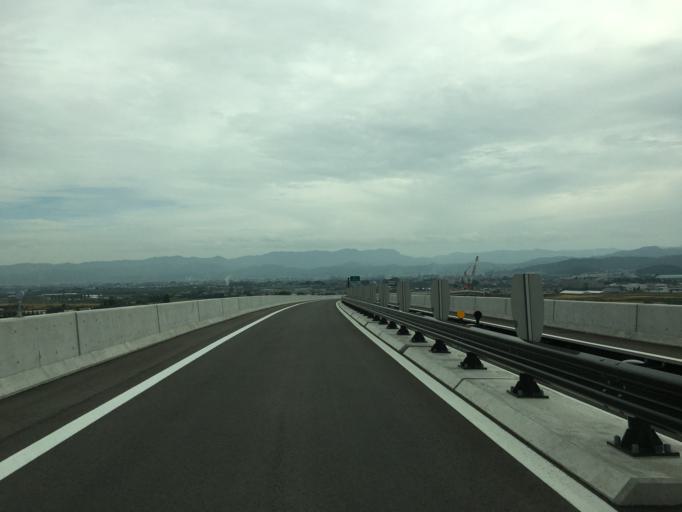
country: JP
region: Fukushima
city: Hobaramachi
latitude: 37.8327
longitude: 140.5007
